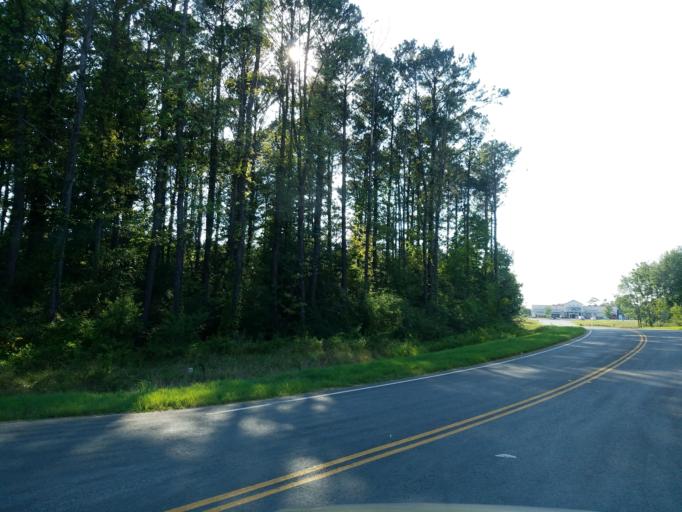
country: US
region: Georgia
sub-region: Bartow County
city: Cartersville
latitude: 34.2088
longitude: -84.7964
